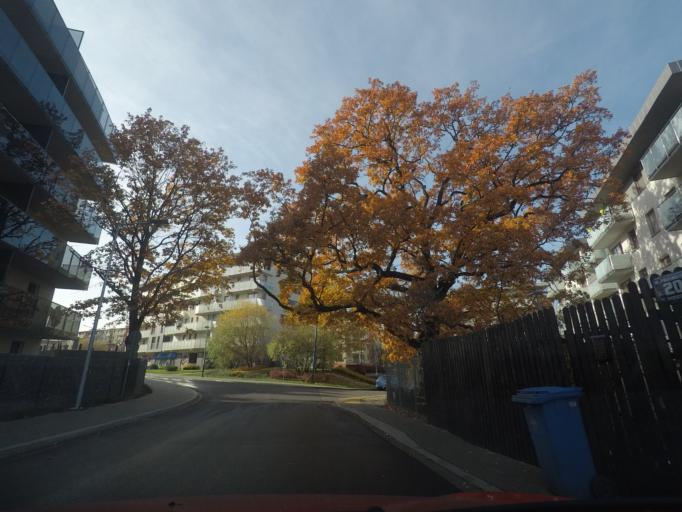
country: PL
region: Lesser Poland Voivodeship
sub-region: Krakow
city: Sidzina
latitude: 50.0220
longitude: 19.9030
